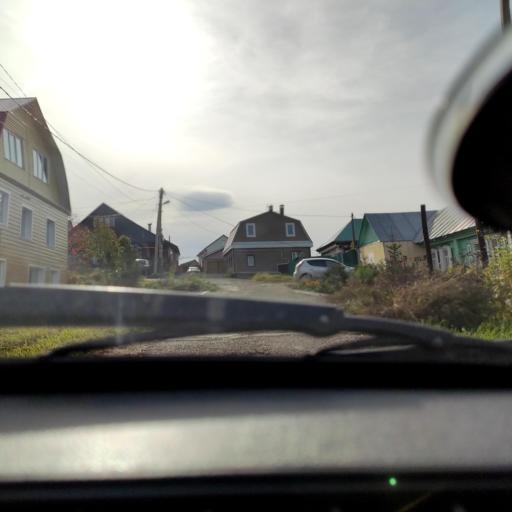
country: RU
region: Bashkortostan
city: Ufa
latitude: 54.7283
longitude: 55.9174
